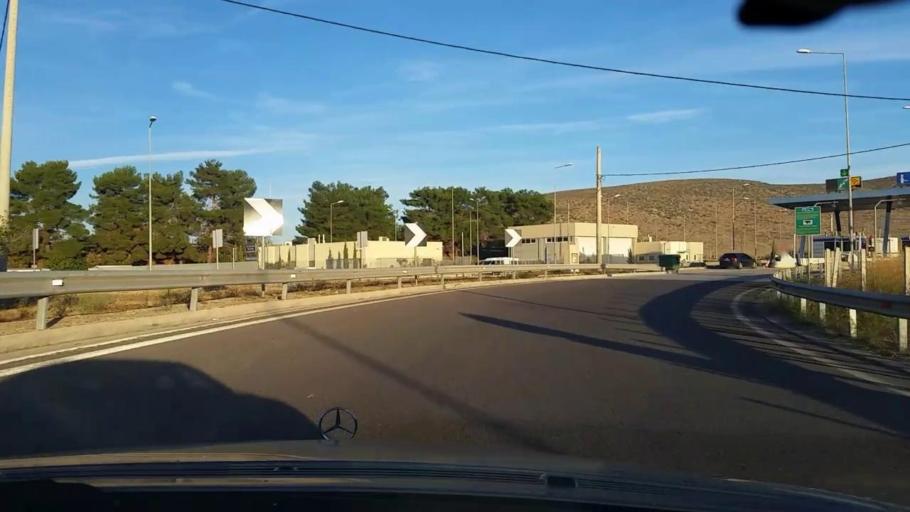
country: GR
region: Central Greece
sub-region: Nomos Voiotias
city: Thivai
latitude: 38.3655
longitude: 23.3250
